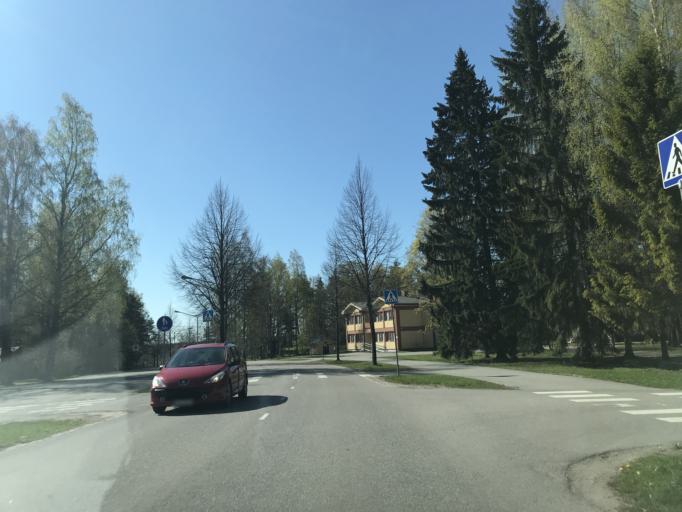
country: FI
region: Paijanne Tavastia
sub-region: Lahti
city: Orimattila
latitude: 60.8098
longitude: 25.7362
